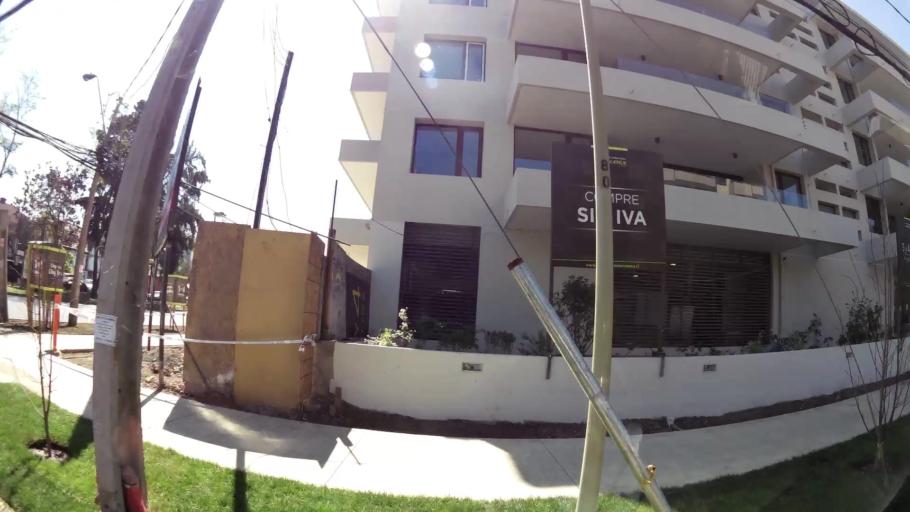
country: CL
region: Santiago Metropolitan
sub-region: Provincia de Santiago
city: Villa Presidente Frei, Nunoa, Santiago, Chile
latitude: -33.4208
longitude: -70.5642
